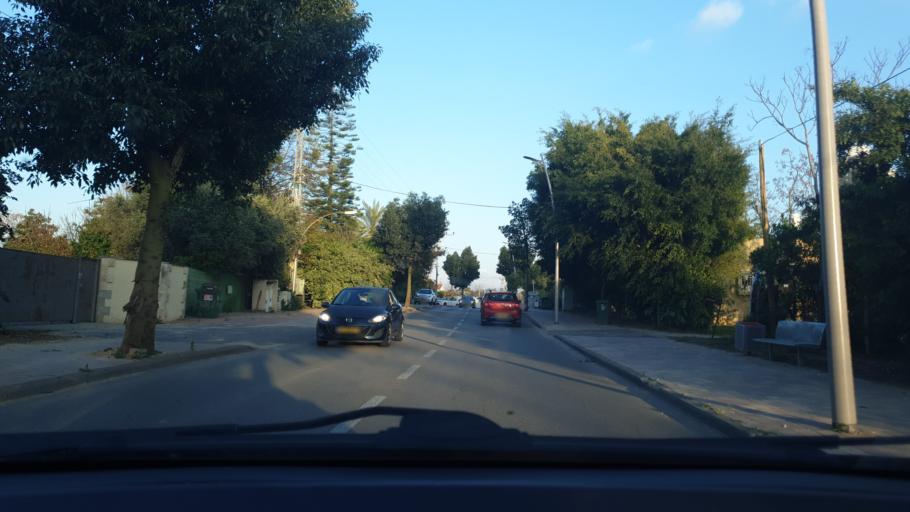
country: IL
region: Central District
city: Ramla
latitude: 31.9358
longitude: 34.8470
